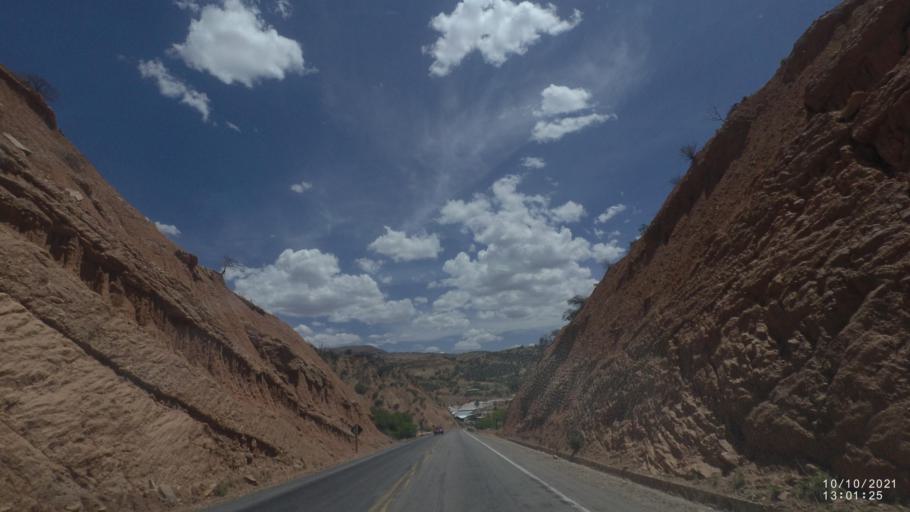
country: BO
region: Cochabamba
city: Sipe Sipe
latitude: -17.5886
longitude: -66.3504
